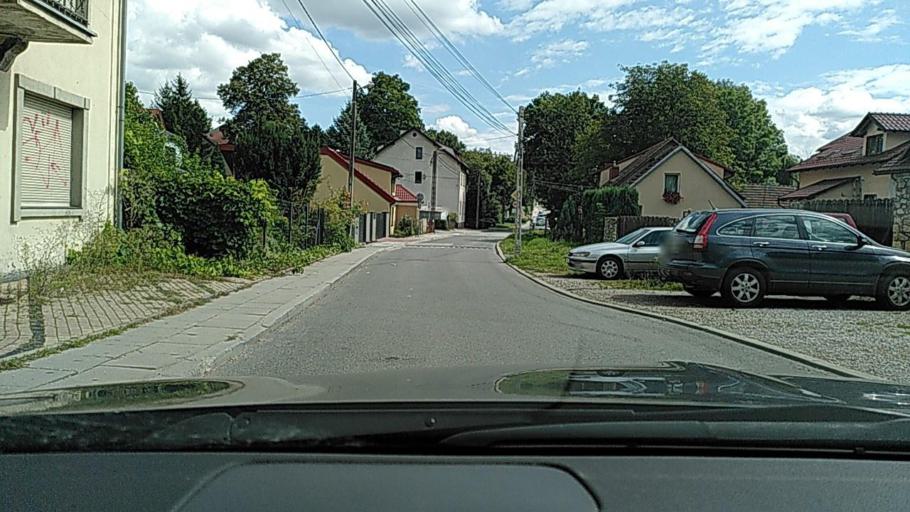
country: PL
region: Lesser Poland Voivodeship
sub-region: Powiat krakowski
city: Rzaska
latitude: 50.0871
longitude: 19.8781
